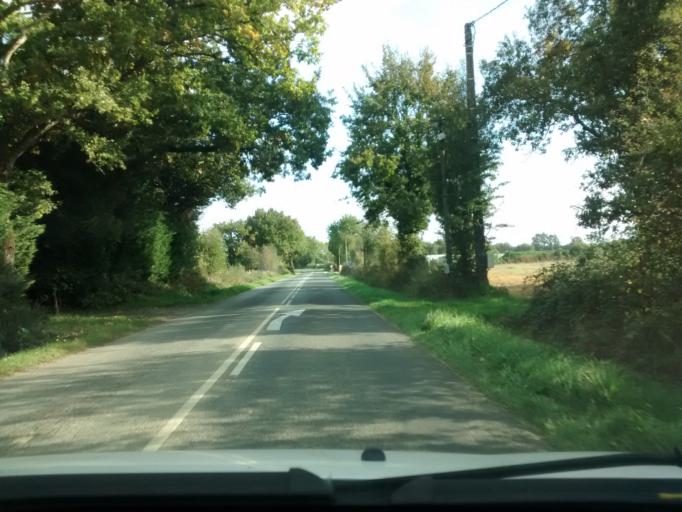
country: FR
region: Pays de la Loire
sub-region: Departement de la Loire-Atlantique
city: Sautron
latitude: 47.2859
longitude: -1.6536
